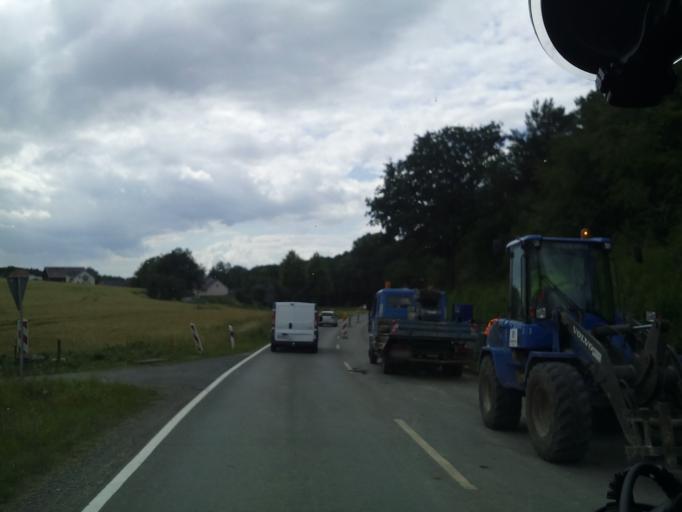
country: DE
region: Bavaria
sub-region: Upper Franconia
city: Rodental
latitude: 50.2728
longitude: 11.0877
